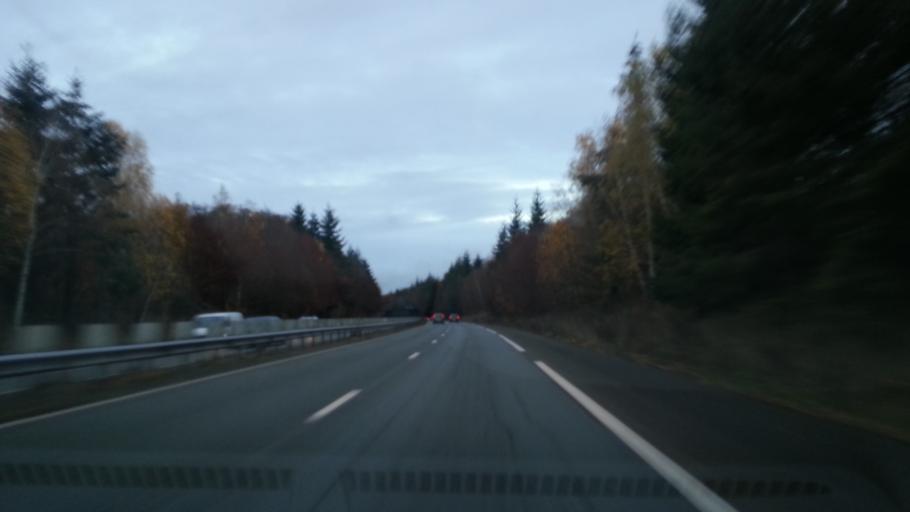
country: FR
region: Picardie
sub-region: Departement de l'Oise
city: Agnetz
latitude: 49.4029
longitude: 2.3695
